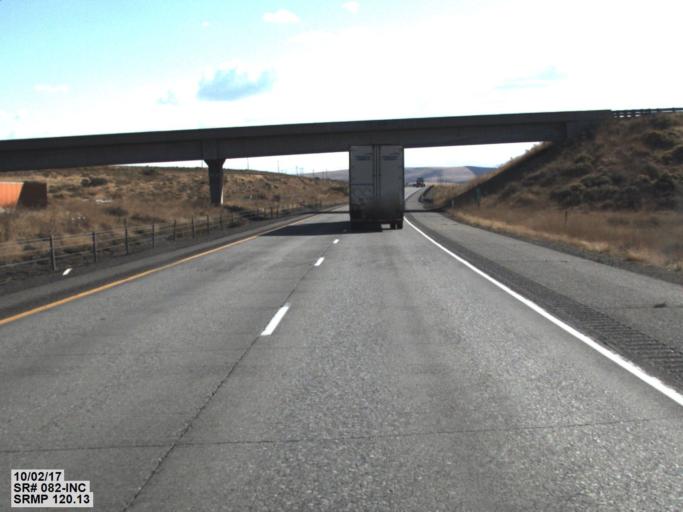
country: US
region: Washington
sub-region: Benton County
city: Highland
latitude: 46.0634
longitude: -119.2237
